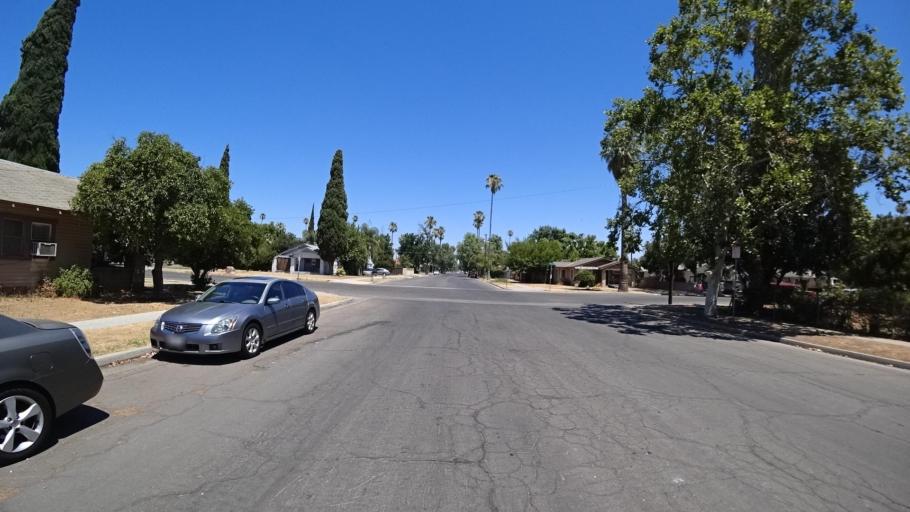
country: US
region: California
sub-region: Fresno County
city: Fresno
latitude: 36.7379
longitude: -119.7578
